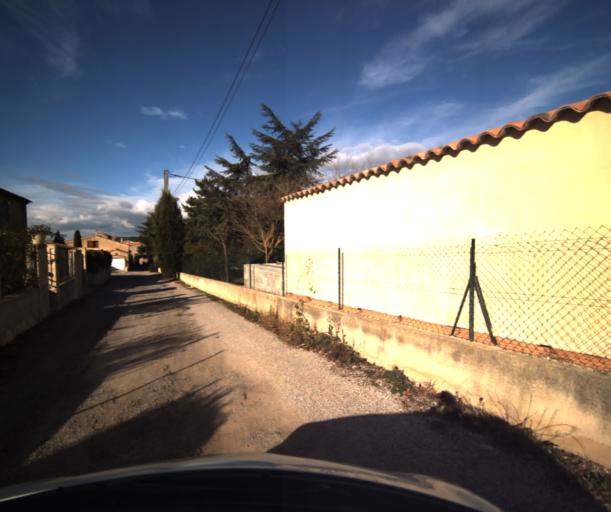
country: FR
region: Provence-Alpes-Cote d'Azur
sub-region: Departement du Vaucluse
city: Pertuis
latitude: 43.6923
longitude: 5.5204
